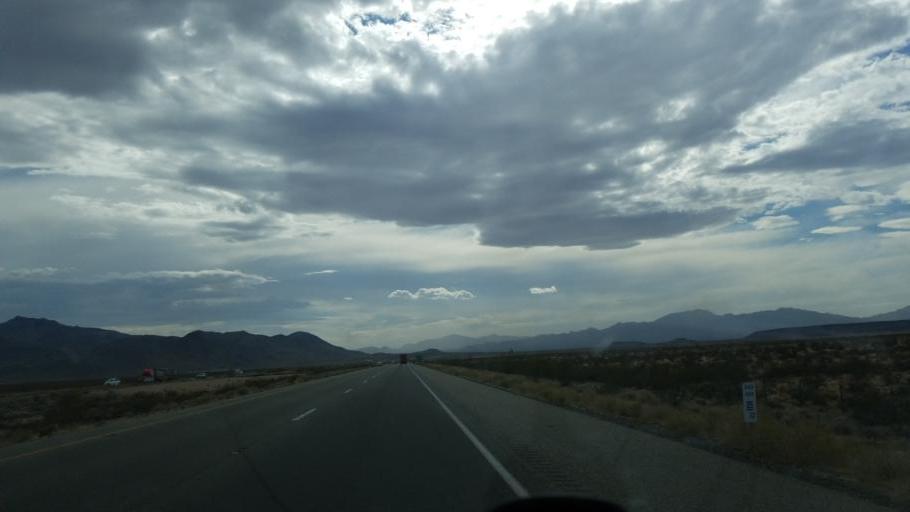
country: US
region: California
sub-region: San Bernardino County
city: Needles
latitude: 34.8038
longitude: -115.2890
